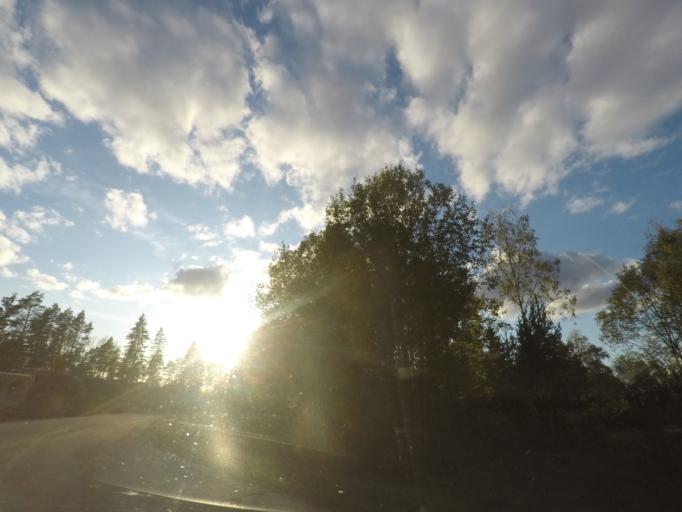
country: SE
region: Vaestmanland
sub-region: Kopings Kommun
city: Koping
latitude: 59.5105
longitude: 16.0632
